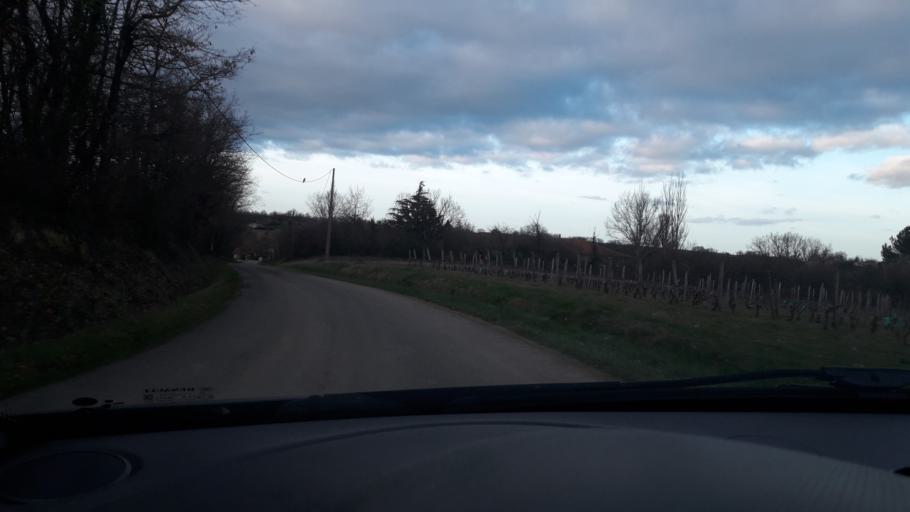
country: FR
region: Midi-Pyrenees
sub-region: Departement de la Haute-Garonne
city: Launac
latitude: 43.7280
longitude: 1.1068
